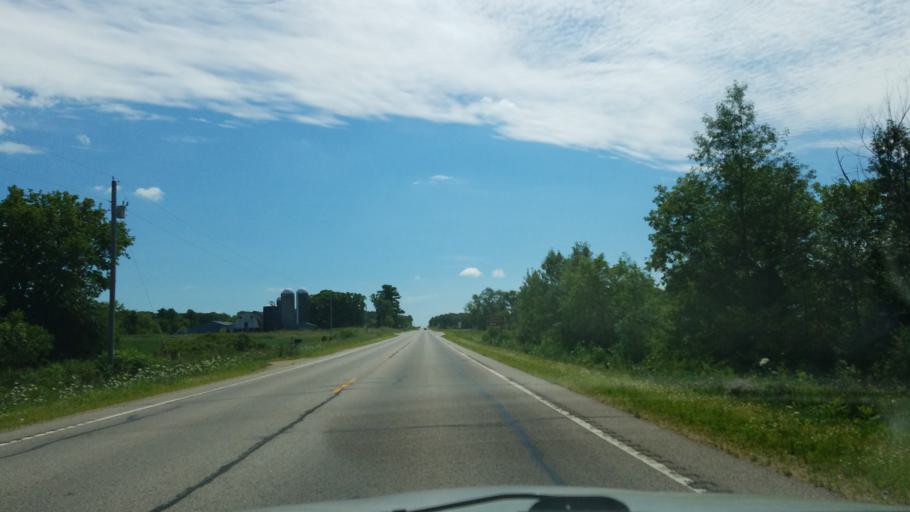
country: US
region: Wisconsin
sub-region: Saint Croix County
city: Glenwood City
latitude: 44.9903
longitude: -92.1966
